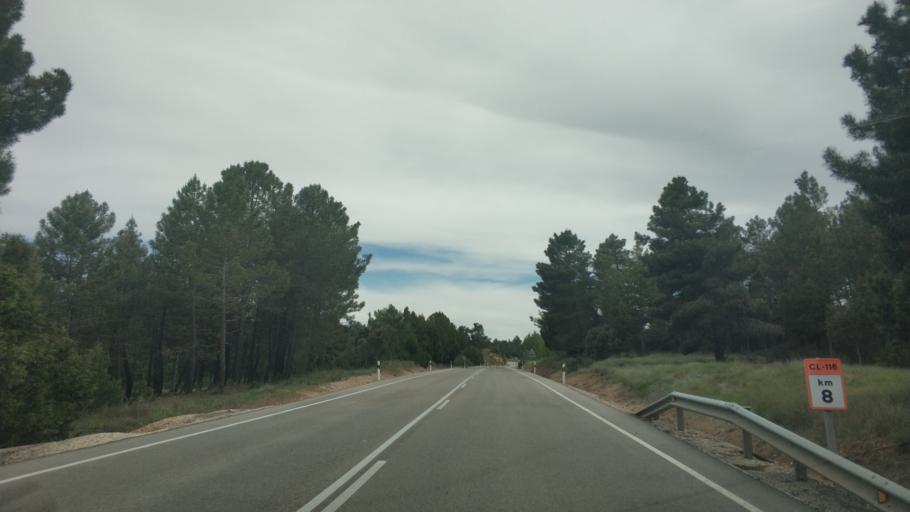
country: ES
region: Castille and Leon
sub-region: Provincia de Soria
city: Valdenebro
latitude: 41.5519
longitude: -2.9626
